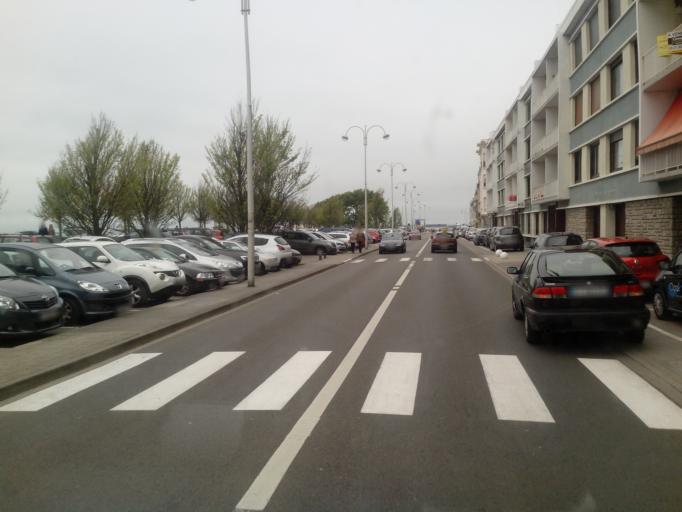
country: FR
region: Nord-Pas-de-Calais
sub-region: Departement du Pas-de-Calais
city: Saint-Martin-Boulogne
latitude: 50.7325
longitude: 1.5951
